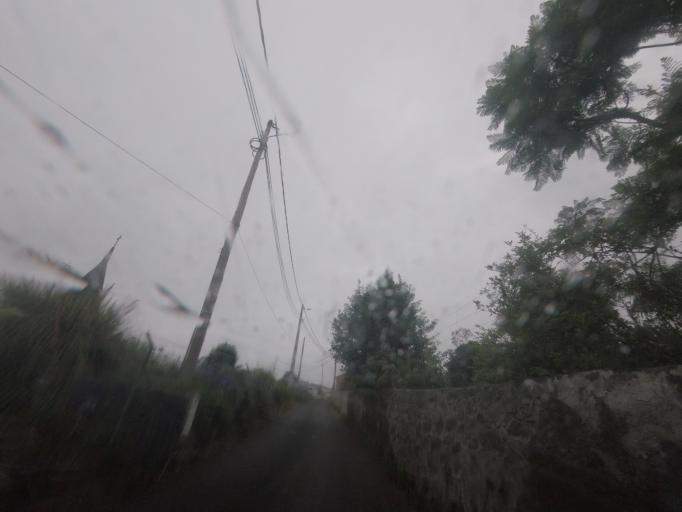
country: PT
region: Madeira
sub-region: Funchal
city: Nossa Senhora do Monte
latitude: 32.6694
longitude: -16.8996
